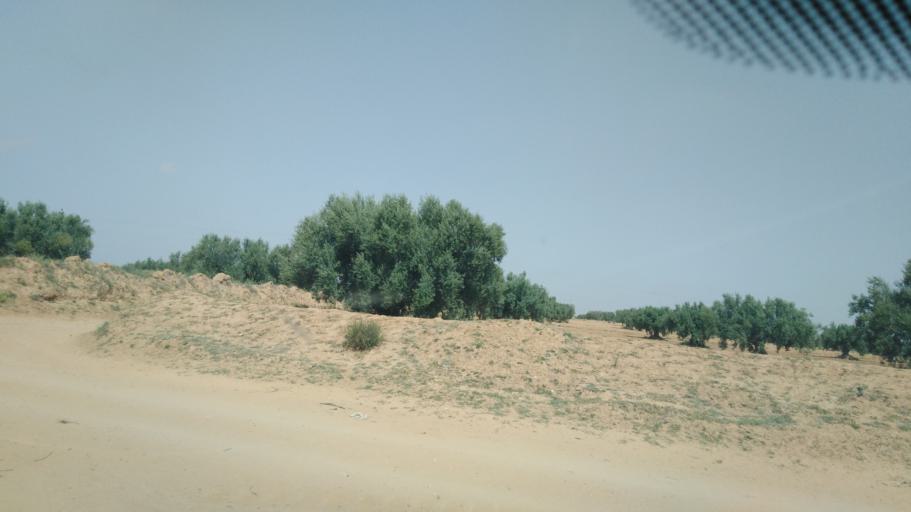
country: TN
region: Safaqis
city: Sfax
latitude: 34.7382
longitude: 10.5728
